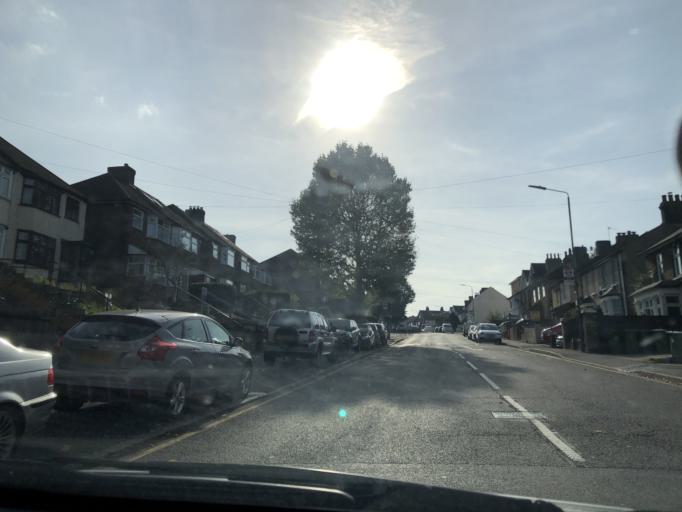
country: GB
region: England
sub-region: Greater London
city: Bexley
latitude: 51.4486
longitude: 0.1812
